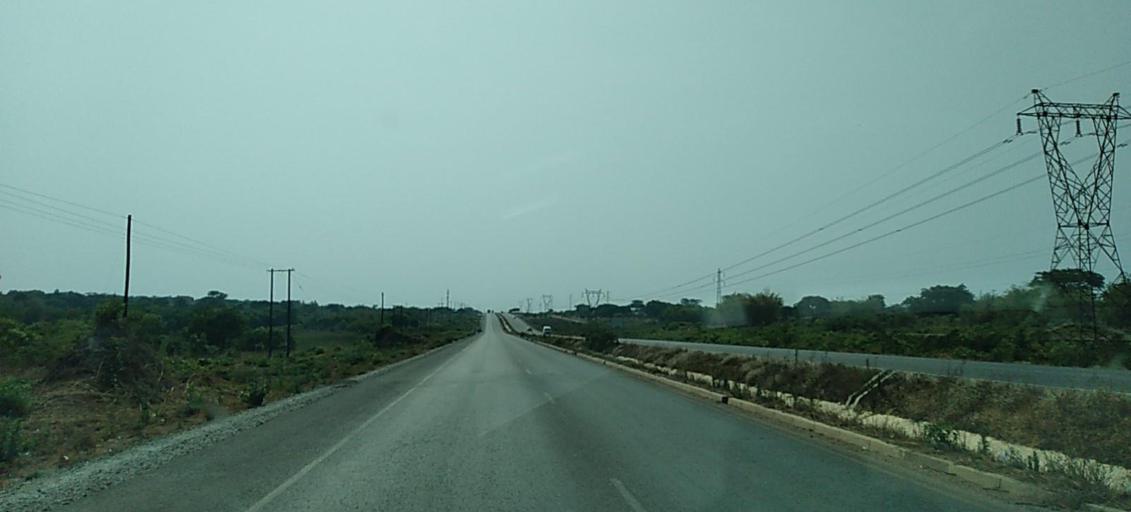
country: ZM
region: Copperbelt
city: Chingola
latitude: -12.5649
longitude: 27.8891
